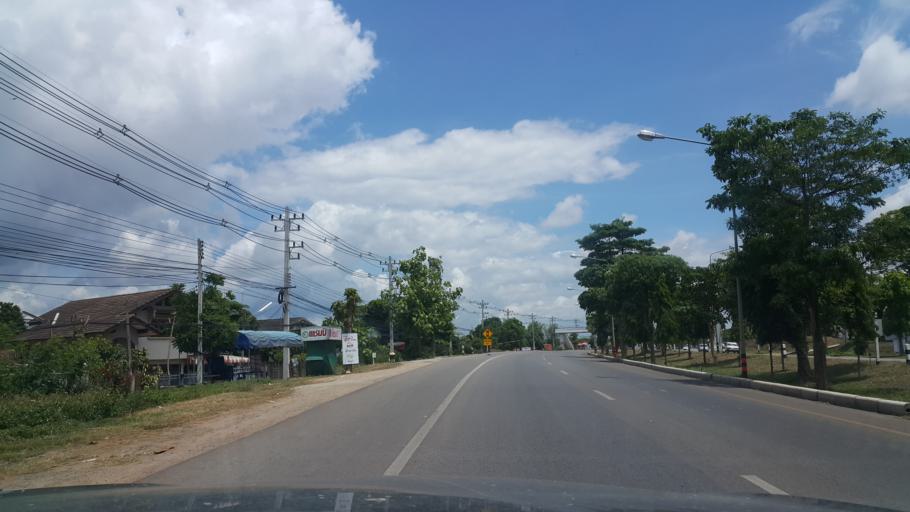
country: TH
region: Phayao
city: Phayao
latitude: 19.1997
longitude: 99.8729
